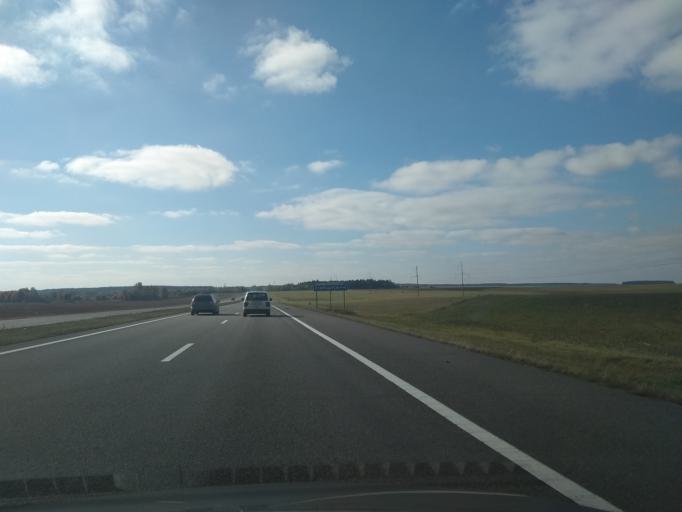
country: BY
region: Minsk
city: Haradzyeya
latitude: 53.3956
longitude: 26.5354
